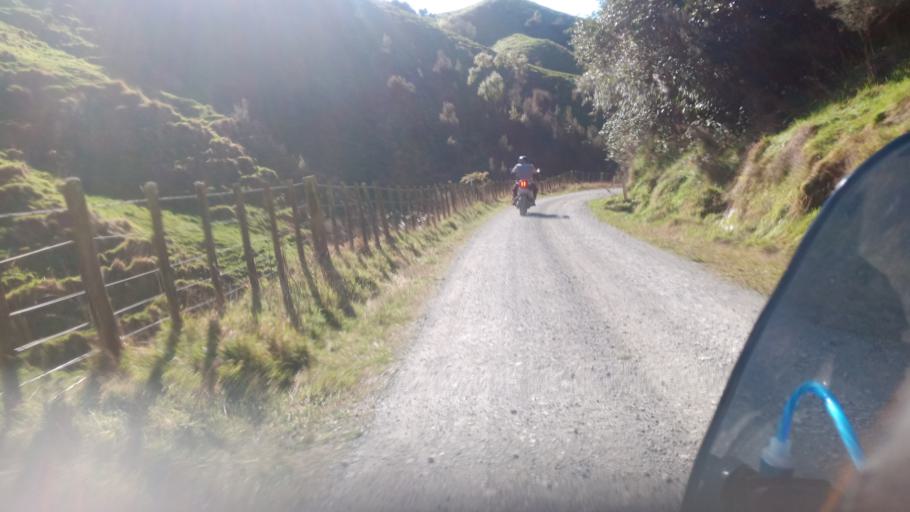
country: NZ
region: Hawke's Bay
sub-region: Wairoa District
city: Wairoa
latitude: -38.6625
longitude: 177.4864
